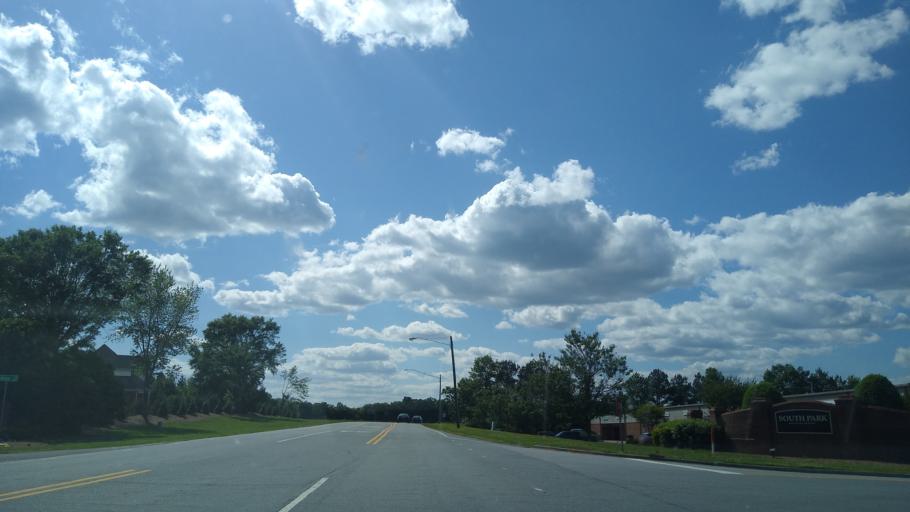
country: US
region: North Carolina
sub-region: Forsyth County
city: Kernersville
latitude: 36.0967
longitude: -80.0736
